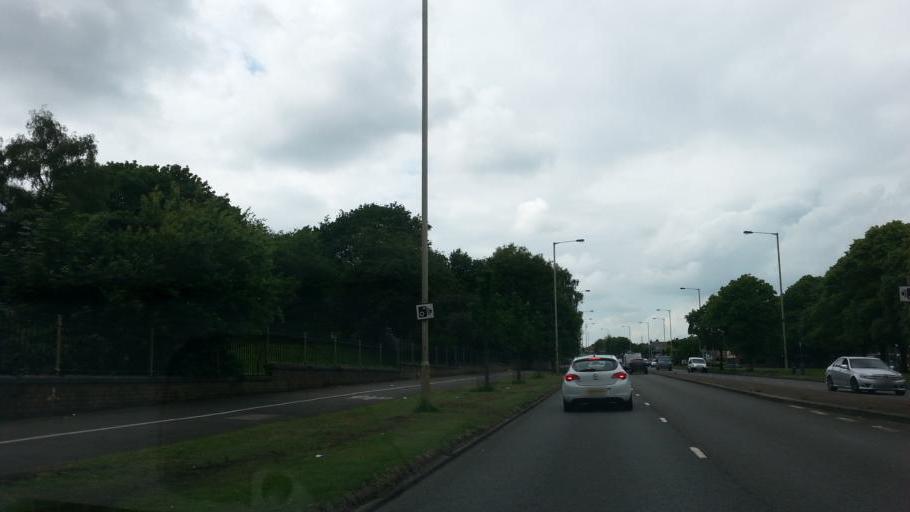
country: GB
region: England
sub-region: Sandwell
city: Tipton
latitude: 52.5381
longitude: -2.0885
